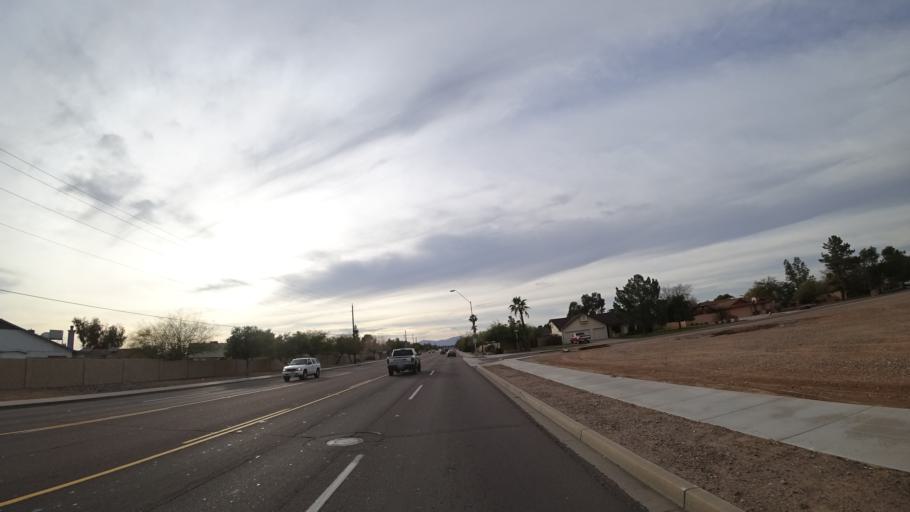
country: US
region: Arizona
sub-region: Maricopa County
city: Peoria
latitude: 33.5664
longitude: -112.2480
